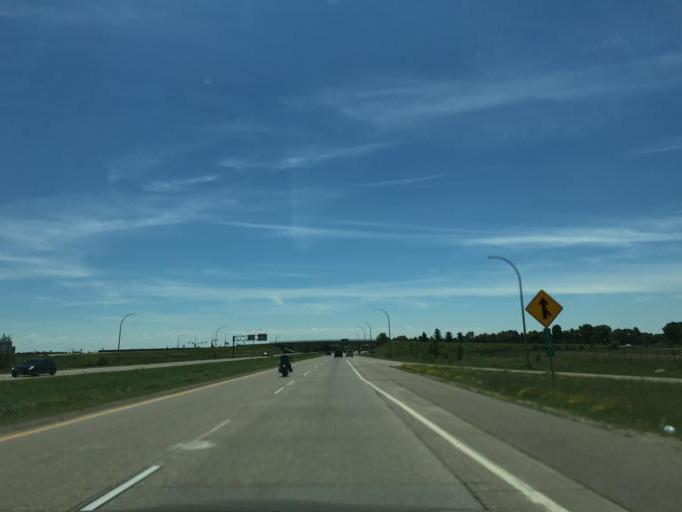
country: US
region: Minnesota
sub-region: Hennepin County
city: Osseo
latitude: 45.1278
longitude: -93.3905
